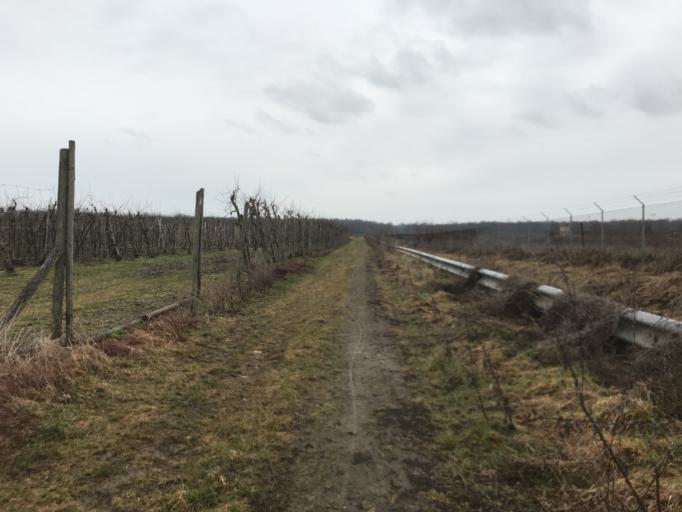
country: DE
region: Rheinland-Pfalz
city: Essenheim
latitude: 49.9718
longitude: 8.1624
